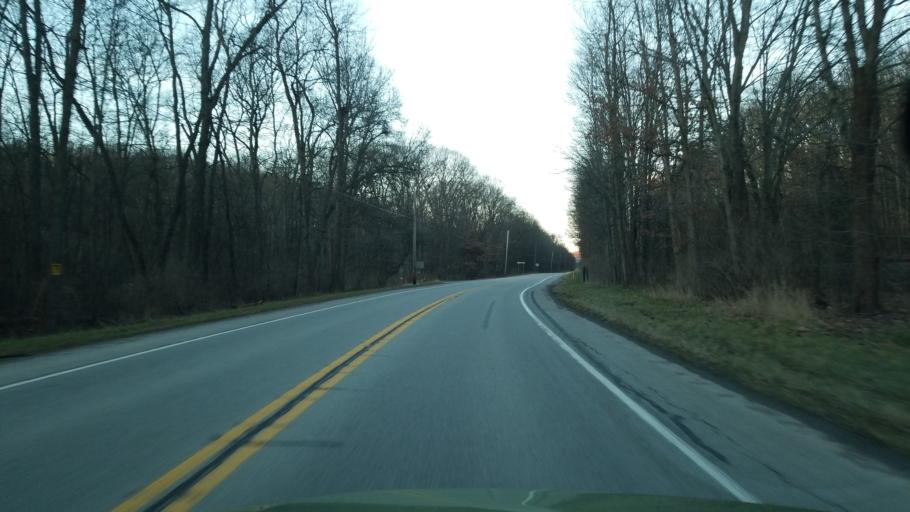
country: US
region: Pennsylvania
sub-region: Indiana County
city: Clymer
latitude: 40.7731
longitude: -79.0579
